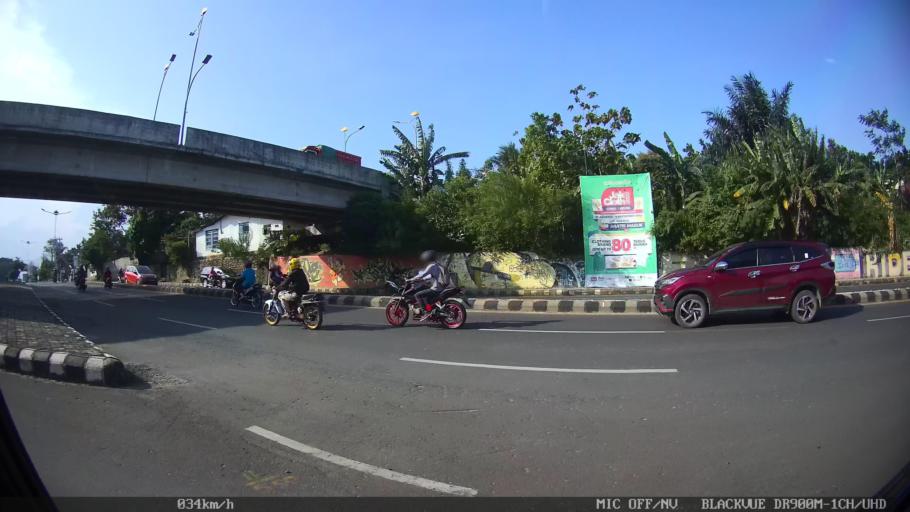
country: ID
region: Lampung
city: Kedaton
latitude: -5.3664
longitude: 105.2305
